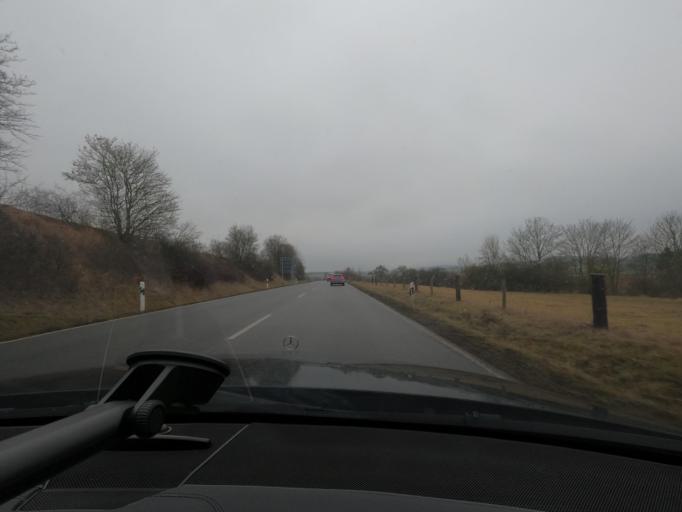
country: DE
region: Hesse
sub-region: Regierungsbezirk Kassel
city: Wolfhagen
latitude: 51.3393
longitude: 9.1384
